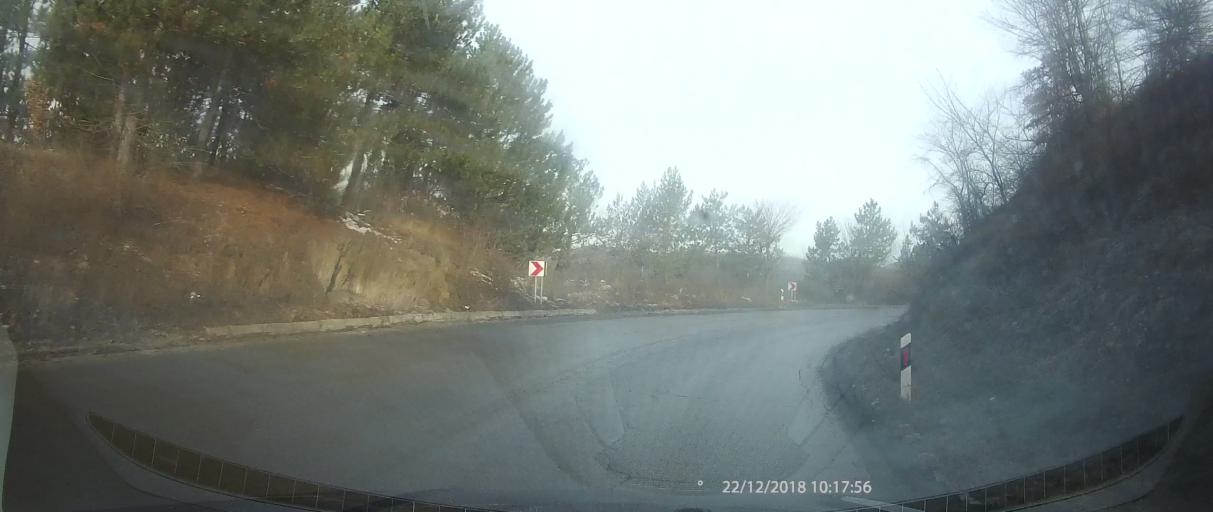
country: MK
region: Kriva Palanka
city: Kriva Palanka
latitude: 42.1843
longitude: 22.2789
